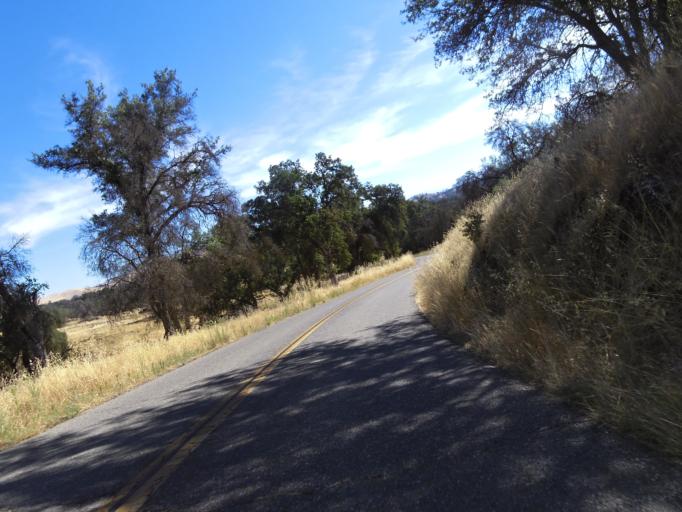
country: US
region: California
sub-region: Mariposa County
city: Mariposa
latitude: 37.2975
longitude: -119.9756
